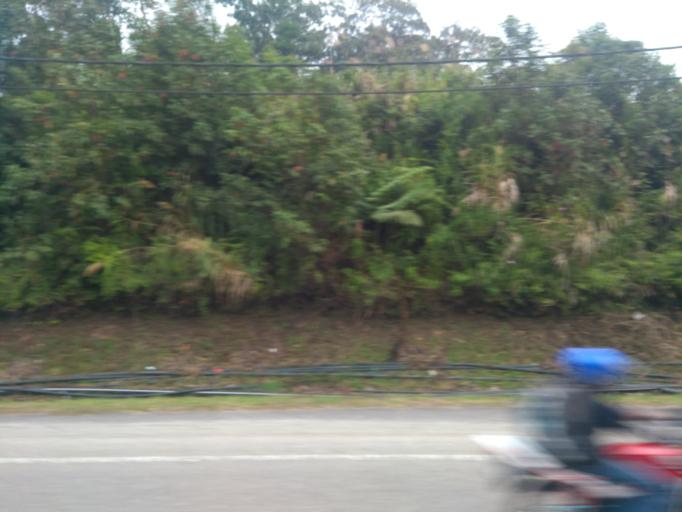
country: MY
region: Pahang
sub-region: Cameron Highlands
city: Tanah Rata
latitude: 4.5830
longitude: 101.3991
